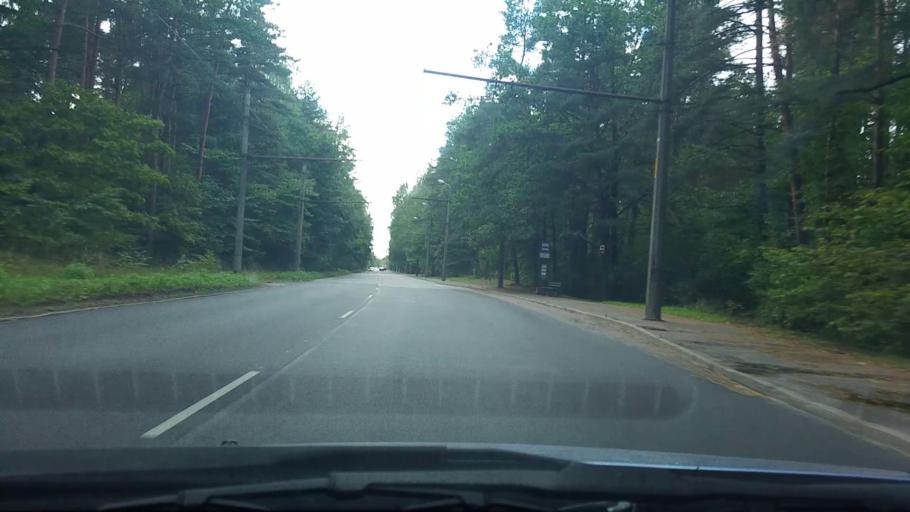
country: LV
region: Riga
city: Jaunciems
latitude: 56.9655
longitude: 24.2080
